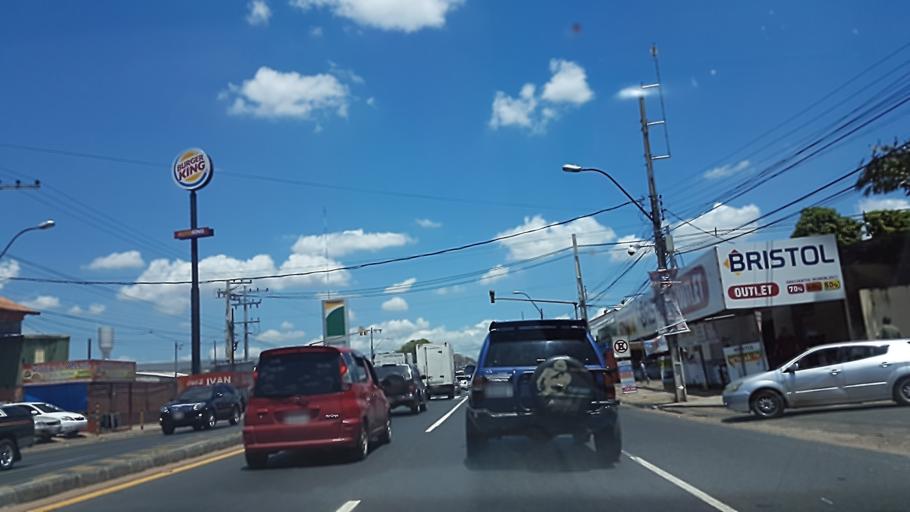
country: PY
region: Central
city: San Lorenzo
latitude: -25.3434
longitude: -57.4893
